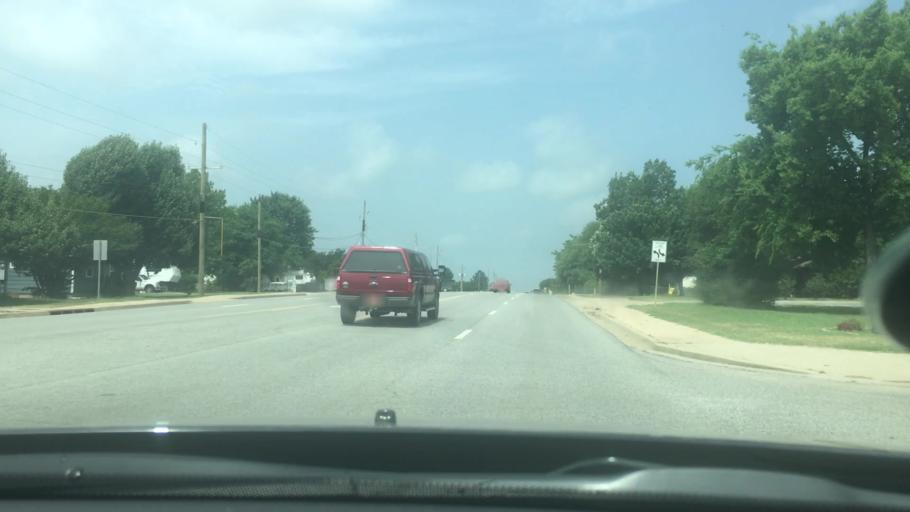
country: US
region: Oklahoma
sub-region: Atoka County
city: Atoka
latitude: 34.3749
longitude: -96.1387
